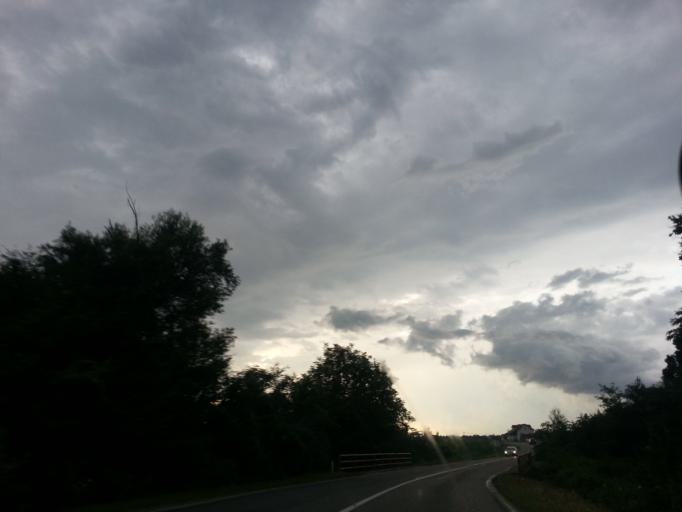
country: BA
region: Republika Srpska
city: Velika Obarska
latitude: 44.8125
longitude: 19.0599
